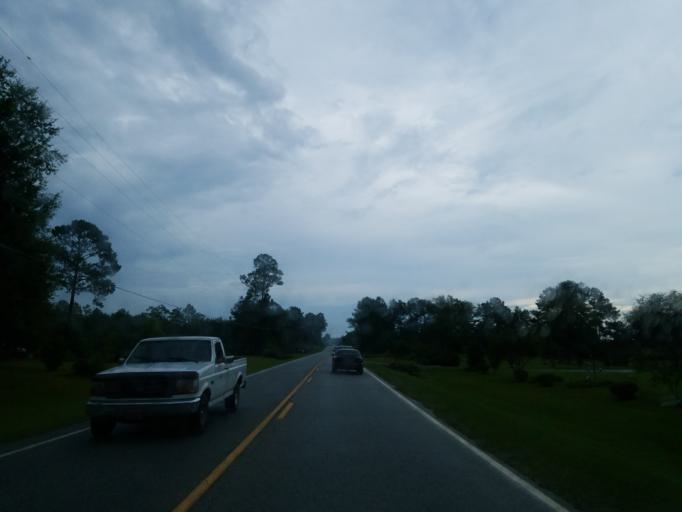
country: US
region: Georgia
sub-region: Berrien County
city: Ray City
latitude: 31.0617
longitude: -83.1588
